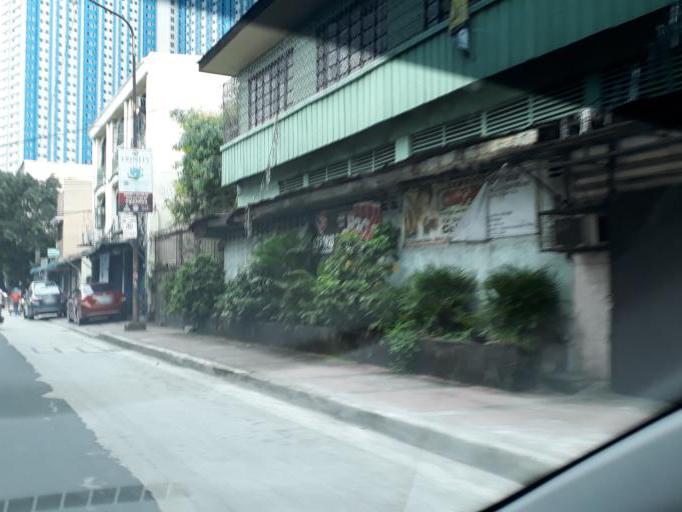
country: PH
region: Metro Manila
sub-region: City of Manila
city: Manila
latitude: 14.6206
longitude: 121.0004
